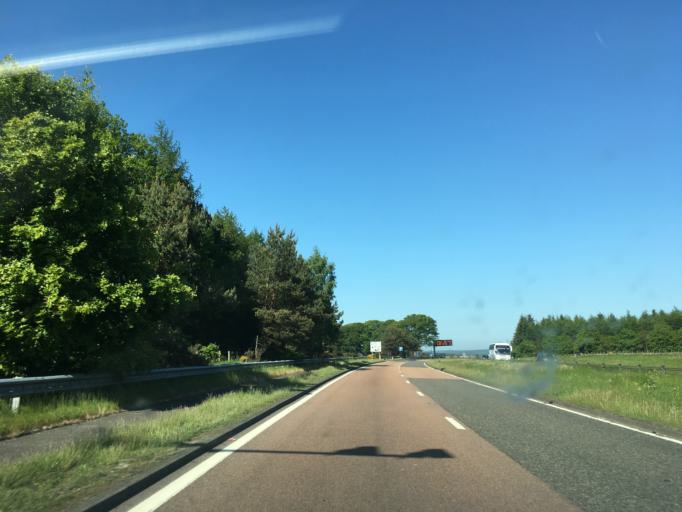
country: GB
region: Scotland
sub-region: Perth and Kinross
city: Perth
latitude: 56.3833
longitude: -3.5074
